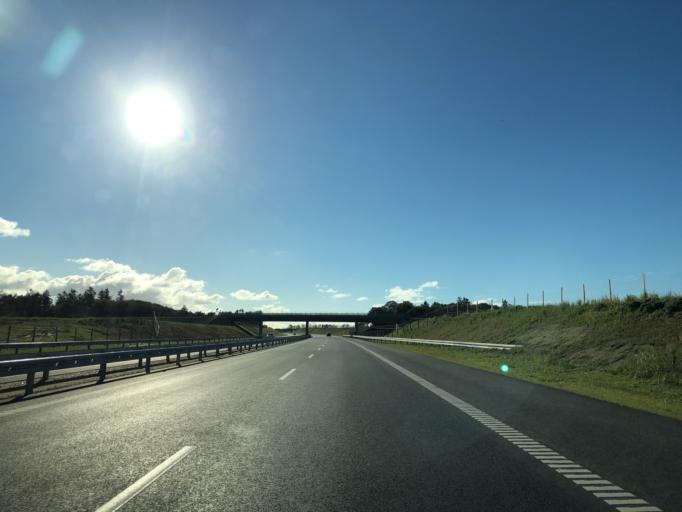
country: DK
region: Central Jutland
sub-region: Herning Kommune
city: Avlum
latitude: 56.3130
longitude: 8.7284
